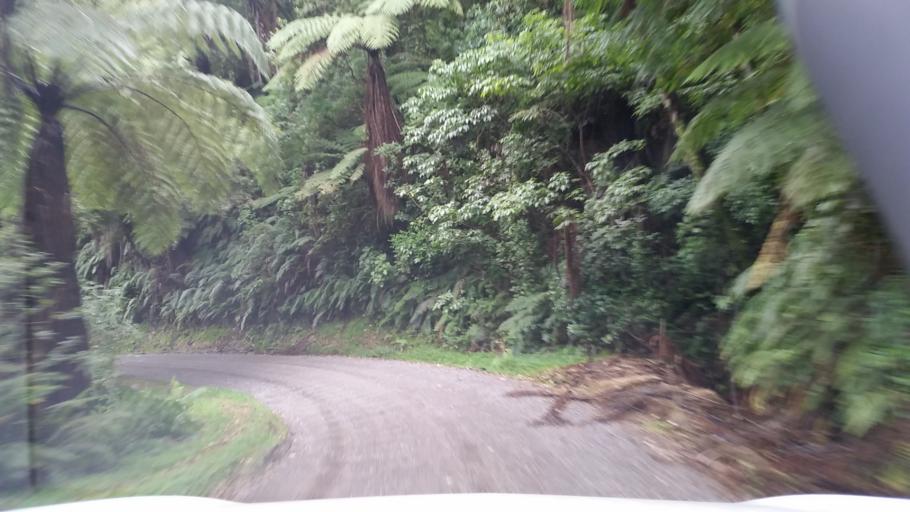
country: NZ
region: Bay of Plenty
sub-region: Rotorua District
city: Rotorua
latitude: -38.1582
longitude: 176.3648
